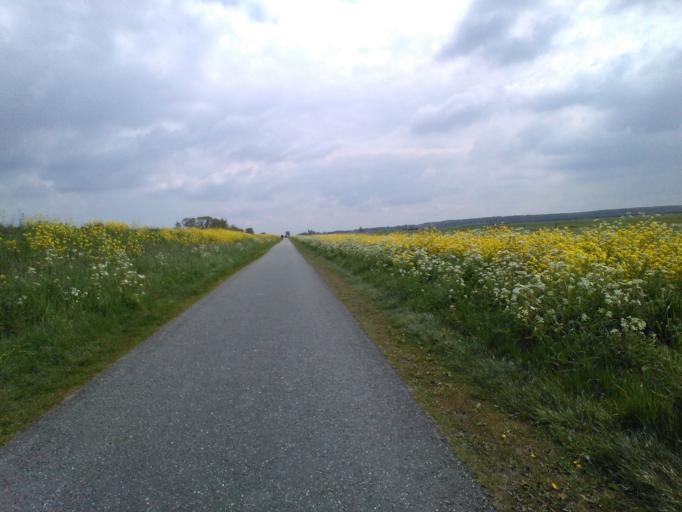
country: NL
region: South Holland
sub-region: Gemeente Maassluis
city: Maassluis
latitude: 51.9298
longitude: 4.2797
